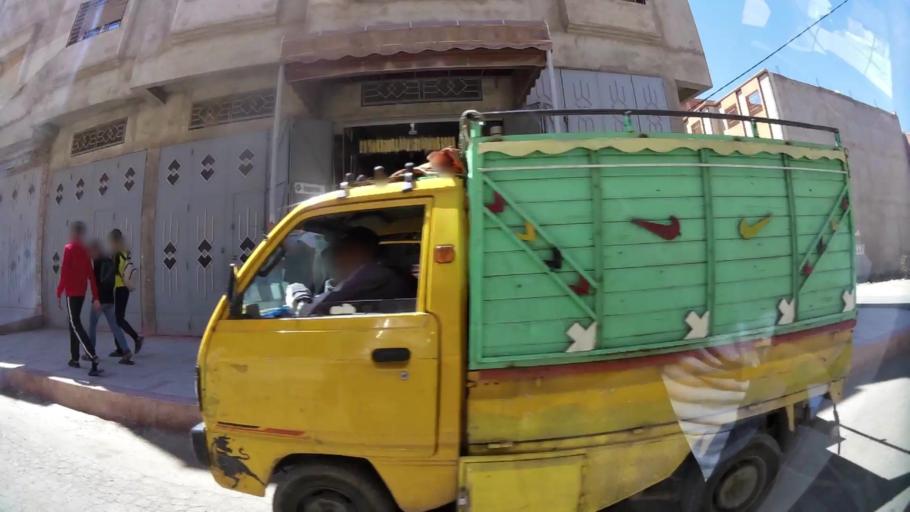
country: MA
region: Oriental
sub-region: Oujda-Angad
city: Oujda
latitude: 34.6879
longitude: -1.9397
